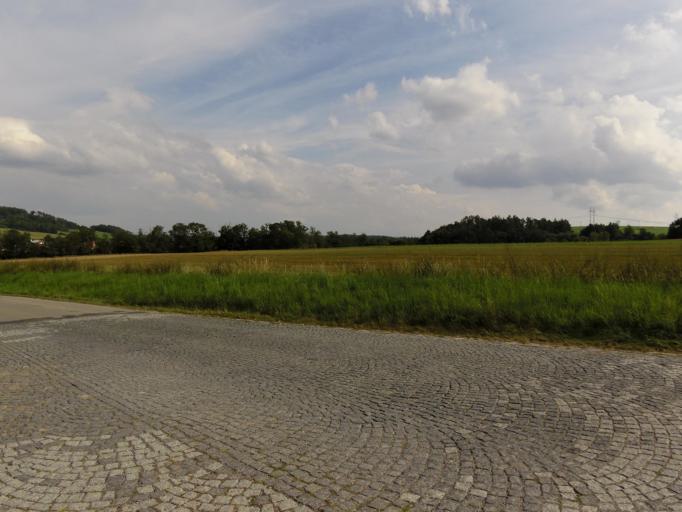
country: CZ
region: Central Bohemia
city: Kamenny Privoz
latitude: 49.8509
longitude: 14.5454
